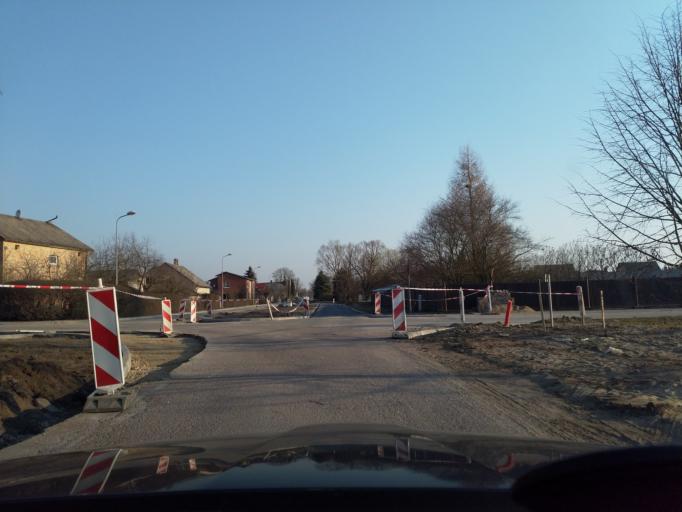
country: LV
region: Grobina
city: Grobina
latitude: 56.5307
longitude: 21.1827
